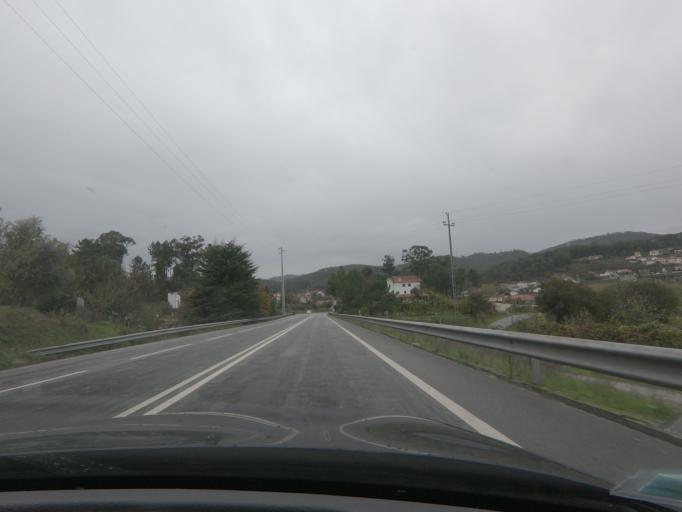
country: PT
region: Porto
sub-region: Amarante
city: Teloes
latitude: 41.2959
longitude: -8.0937
